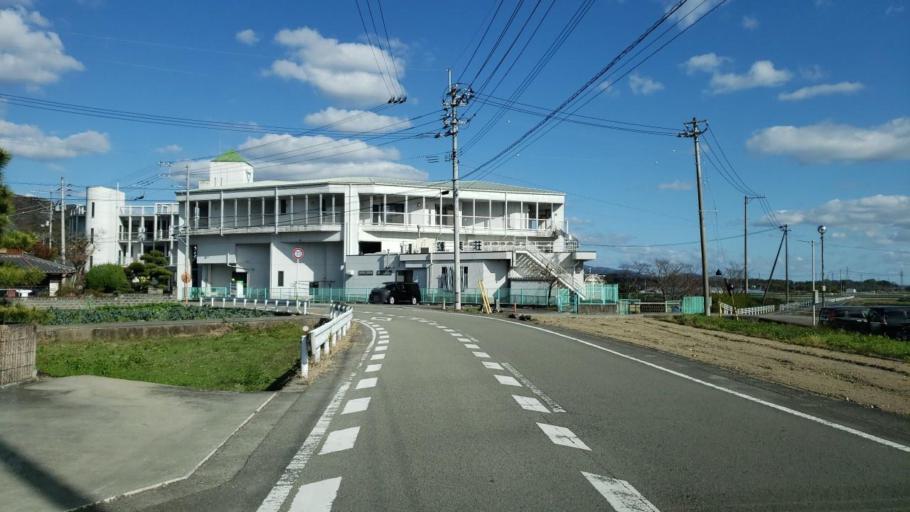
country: JP
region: Tokushima
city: Wakimachi
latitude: 34.0751
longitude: 134.1937
